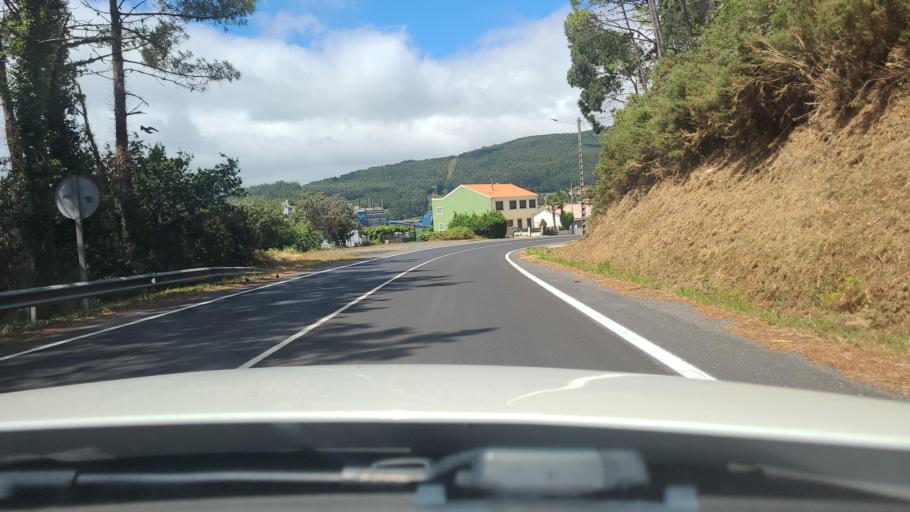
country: ES
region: Galicia
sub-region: Provincia da Coruna
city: Corcubion
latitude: 42.9407
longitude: -9.1731
